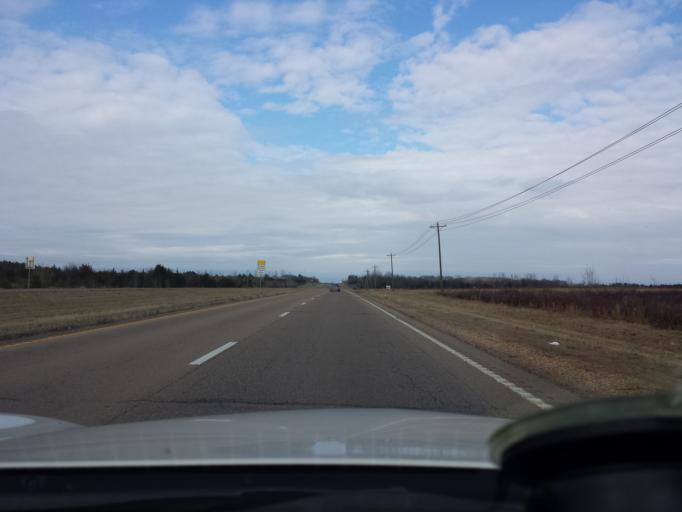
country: US
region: Mississippi
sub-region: Clay County
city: West Point
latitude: 33.5153
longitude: -88.6588
